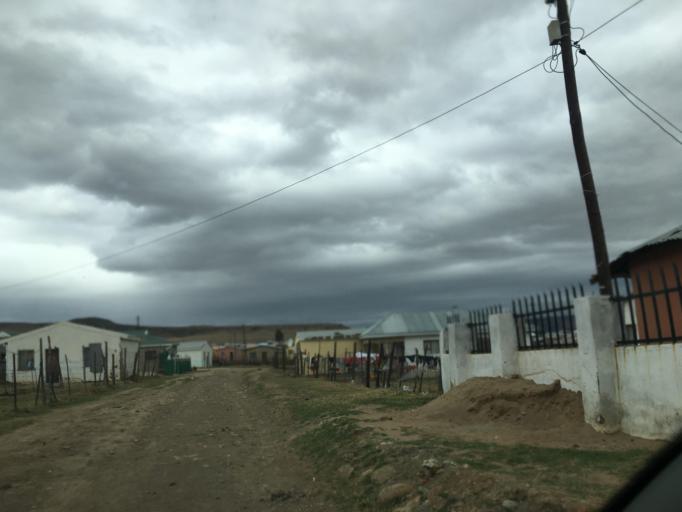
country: ZA
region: Eastern Cape
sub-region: Chris Hani District Municipality
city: Cala
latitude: -31.5355
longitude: 27.7006
